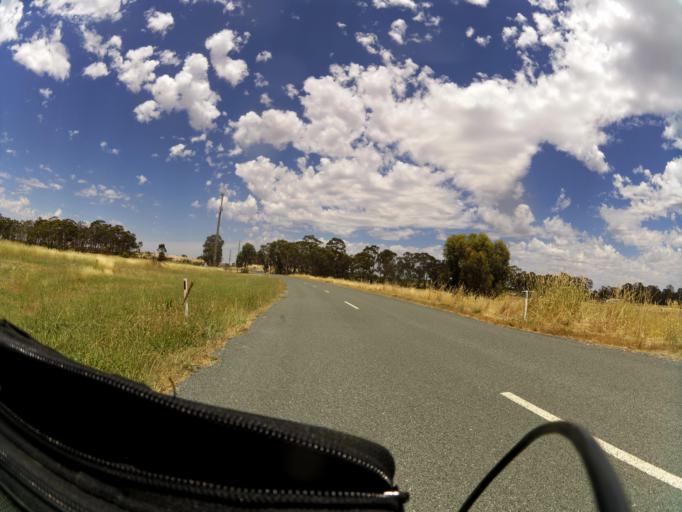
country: AU
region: Victoria
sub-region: Greater Shepparton
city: Shepparton
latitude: -36.6281
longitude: 145.2114
